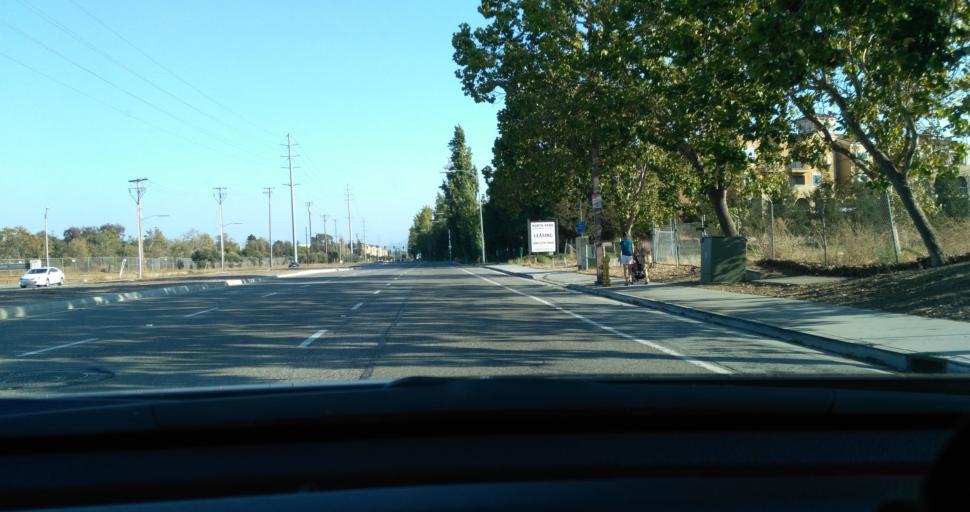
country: US
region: California
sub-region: Santa Clara County
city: Milpitas
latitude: 37.4115
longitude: -121.9370
